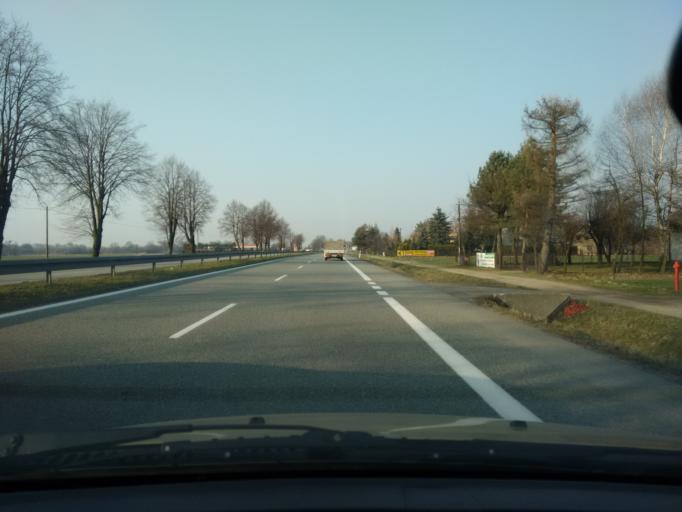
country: PL
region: Silesian Voivodeship
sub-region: Powiat cieszynski
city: Drogomysl
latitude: 49.8768
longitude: 18.7441
